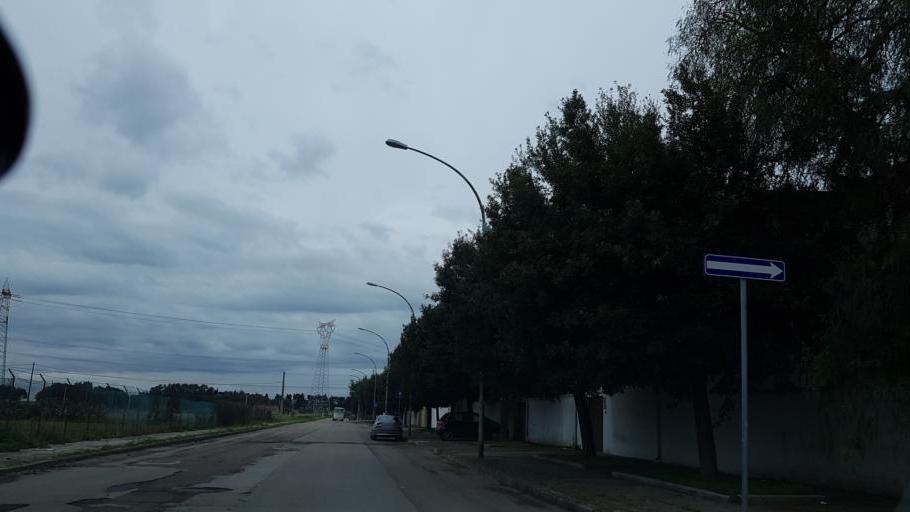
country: IT
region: Apulia
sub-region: Provincia di Brindisi
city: La Rosa
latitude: 40.6070
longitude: 17.9536
